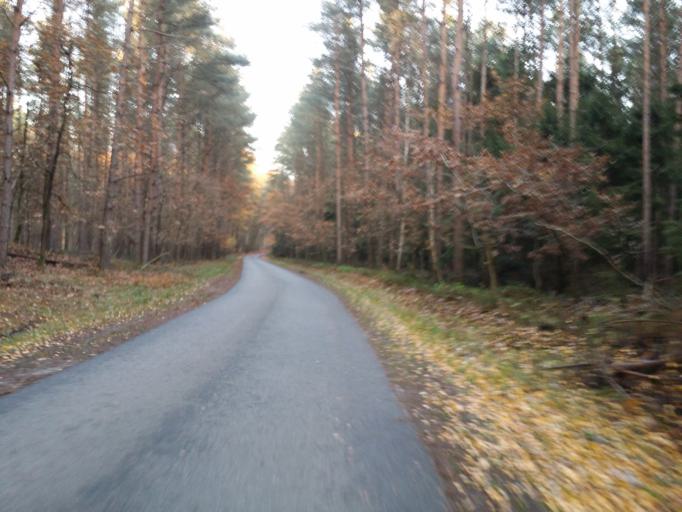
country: DE
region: Lower Saxony
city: Ahausen
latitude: 53.0731
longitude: 9.2914
